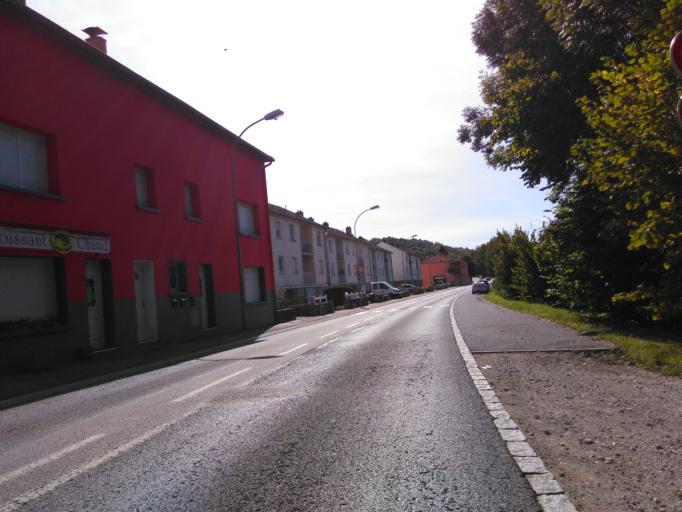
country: FR
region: Lorraine
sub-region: Departement de la Moselle
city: Ottange
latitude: 49.4506
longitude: 6.0258
